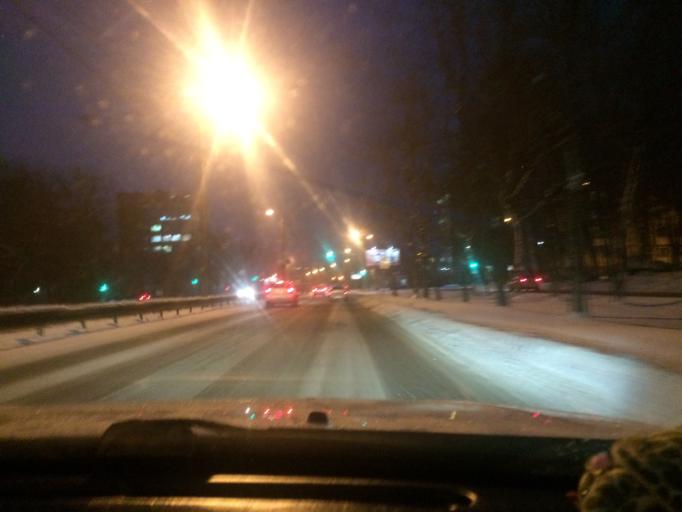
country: RU
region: Tula
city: Mendeleyevskiy
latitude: 54.1559
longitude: 37.5909
